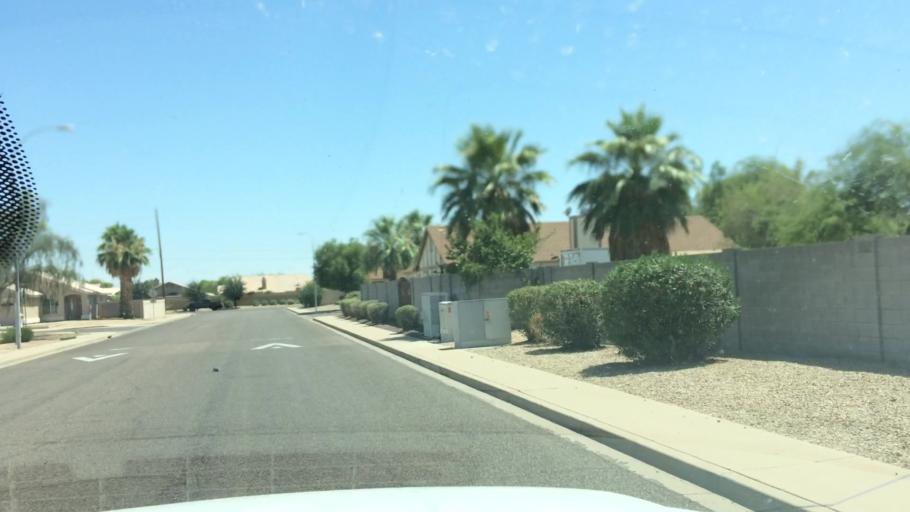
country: US
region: Arizona
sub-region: Maricopa County
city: Peoria
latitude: 33.5967
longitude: -112.2416
